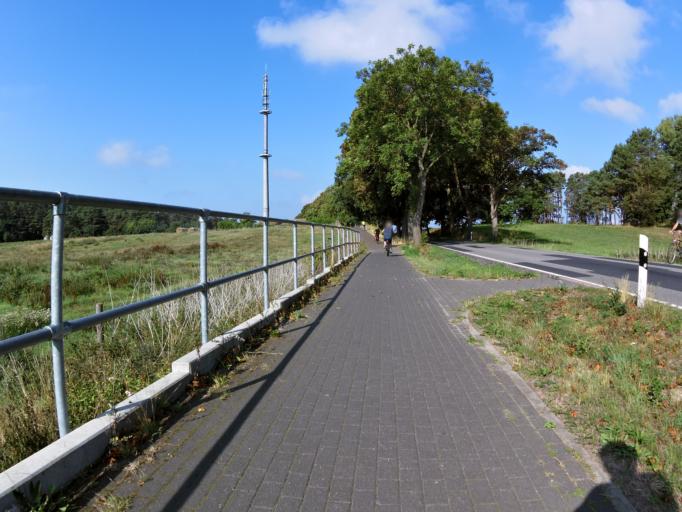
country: DE
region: Mecklenburg-Vorpommern
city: Loddin
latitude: 53.9400
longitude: 14.0518
